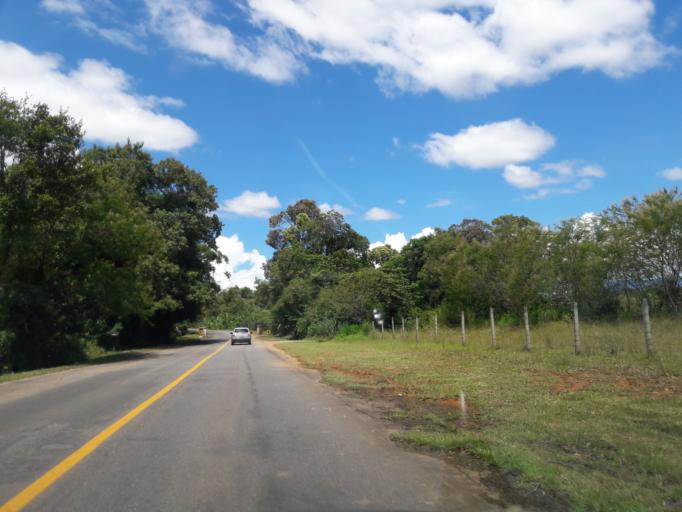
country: BR
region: Parana
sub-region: Antonina
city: Antonina
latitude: -25.4181
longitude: -48.8264
